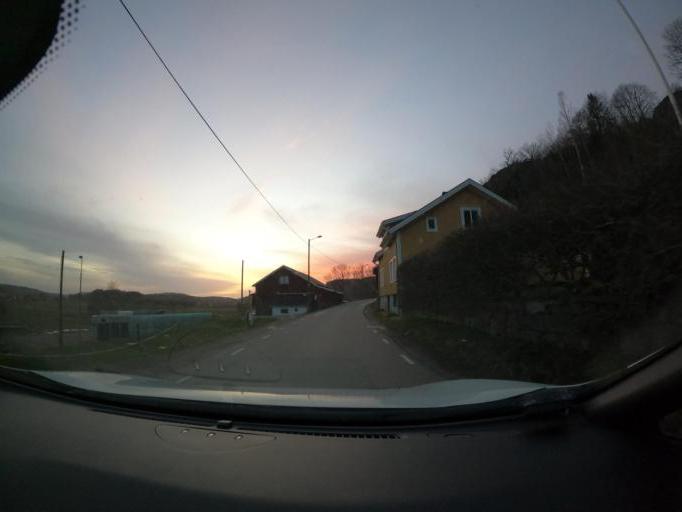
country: SE
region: Vaestra Goetaland
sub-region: Harryda Kommun
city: Molnlycke
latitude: 57.6058
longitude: 12.1576
